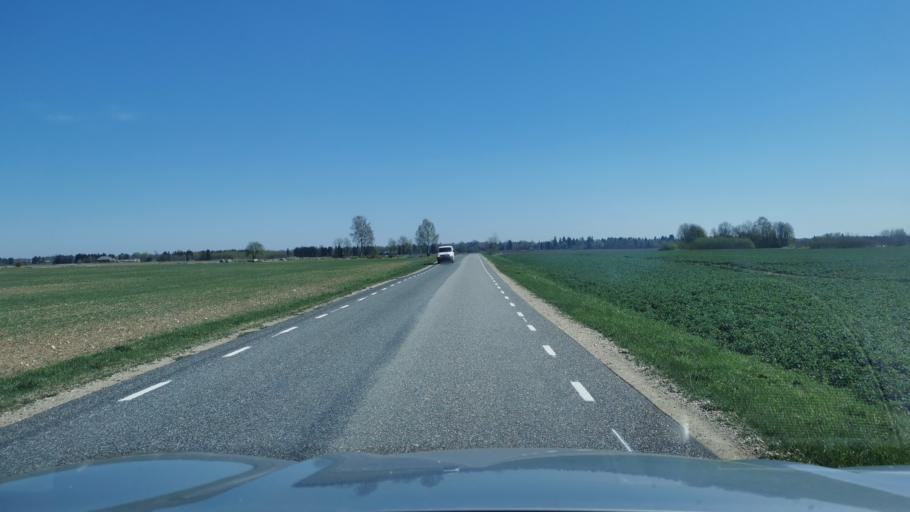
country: EE
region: Laeaene-Virumaa
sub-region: Vinni vald
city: Vinni
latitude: 59.0845
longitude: 26.6013
